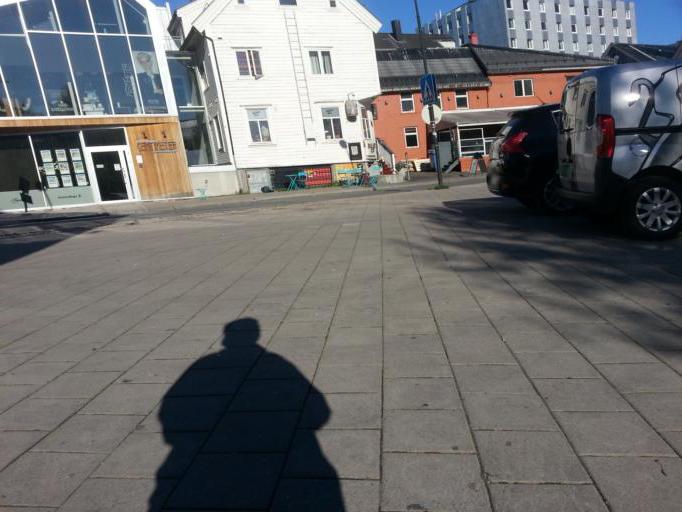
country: NO
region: Troms
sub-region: Tromso
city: Tromso
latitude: 69.6472
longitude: 18.9547
